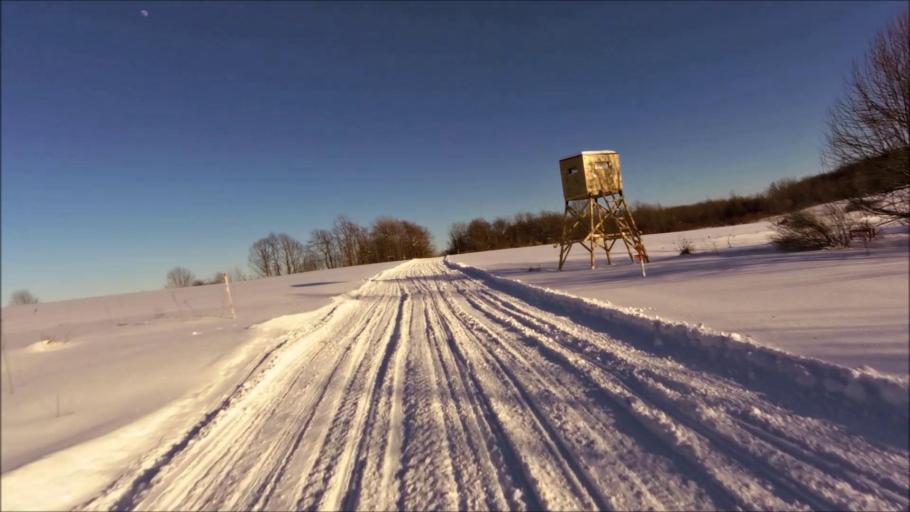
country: US
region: New York
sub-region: Chautauqua County
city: Lakewood
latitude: 42.2271
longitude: -79.3444
